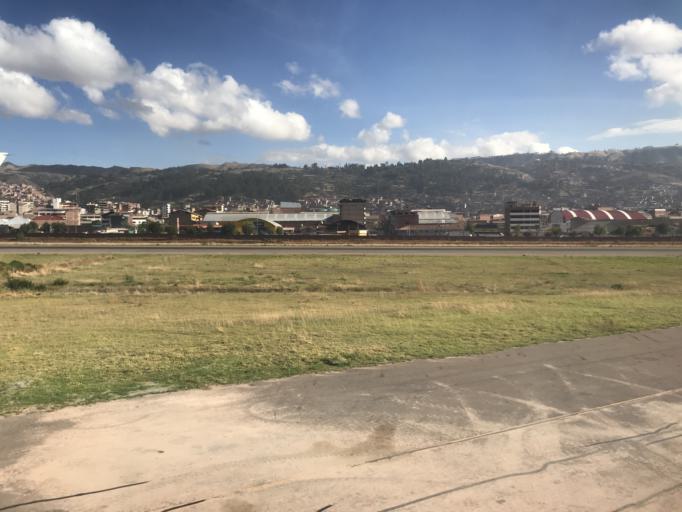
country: PE
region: Cusco
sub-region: Provincia de Cusco
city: Cusco
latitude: -13.5366
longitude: -71.9417
